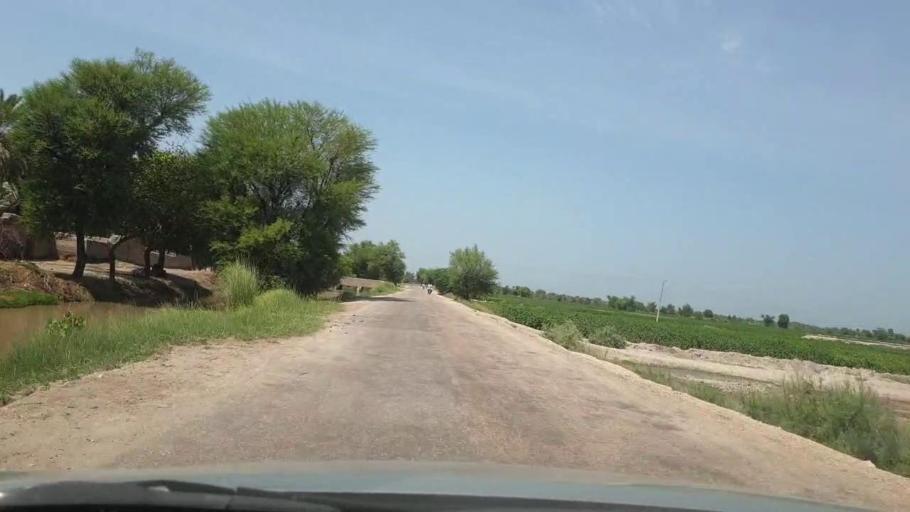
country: PK
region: Sindh
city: Pano Aqil
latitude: 27.6744
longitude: 69.1090
